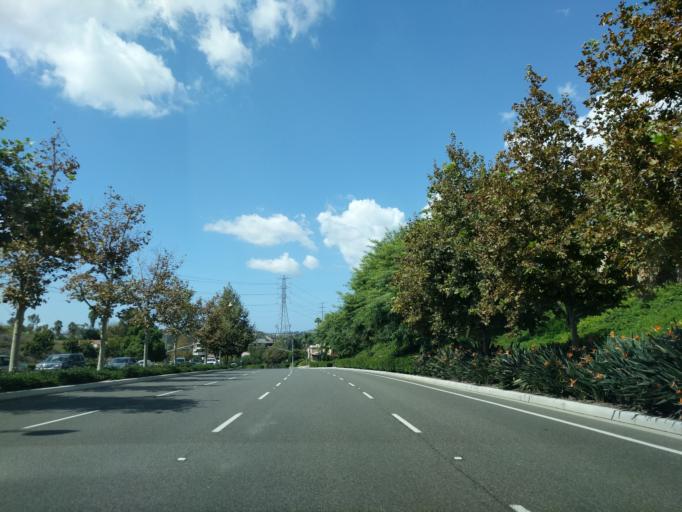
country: US
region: California
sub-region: Orange County
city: Ladera Ranch
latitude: 33.5642
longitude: -117.6606
